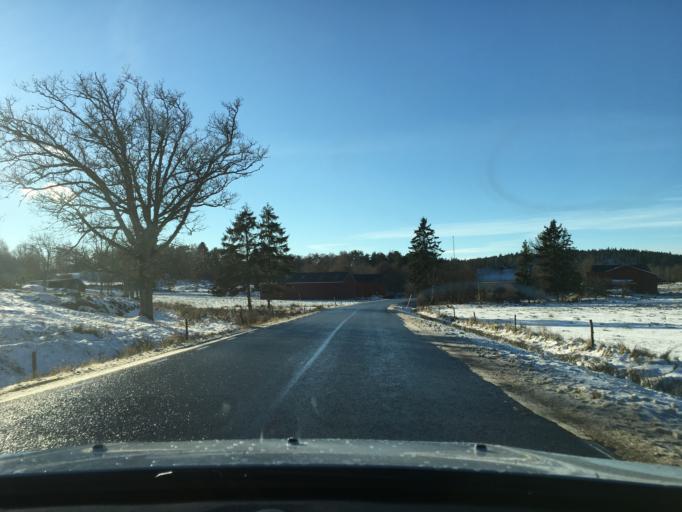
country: SE
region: Vaestra Goetaland
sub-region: Tjorns Kommun
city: Myggenas
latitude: 58.1237
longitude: 11.7447
